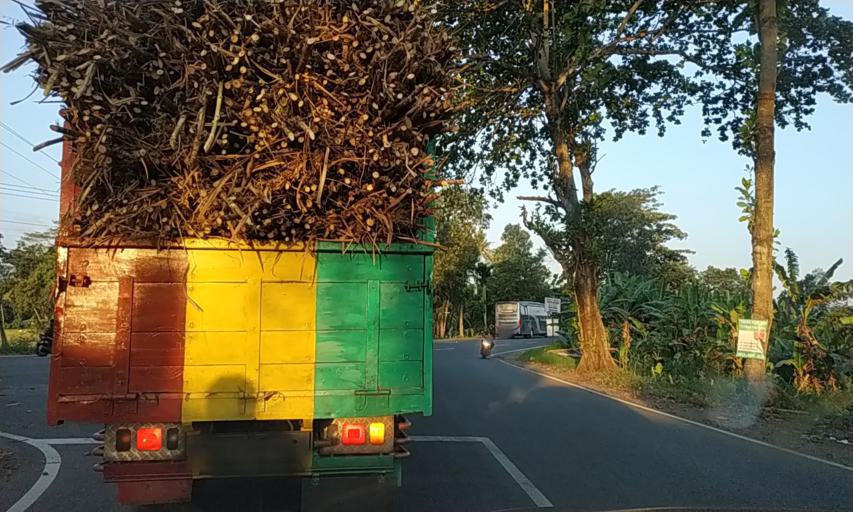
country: ID
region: Daerah Istimewa Yogyakarta
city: Srandakan
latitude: -7.8835
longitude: 110.0472
